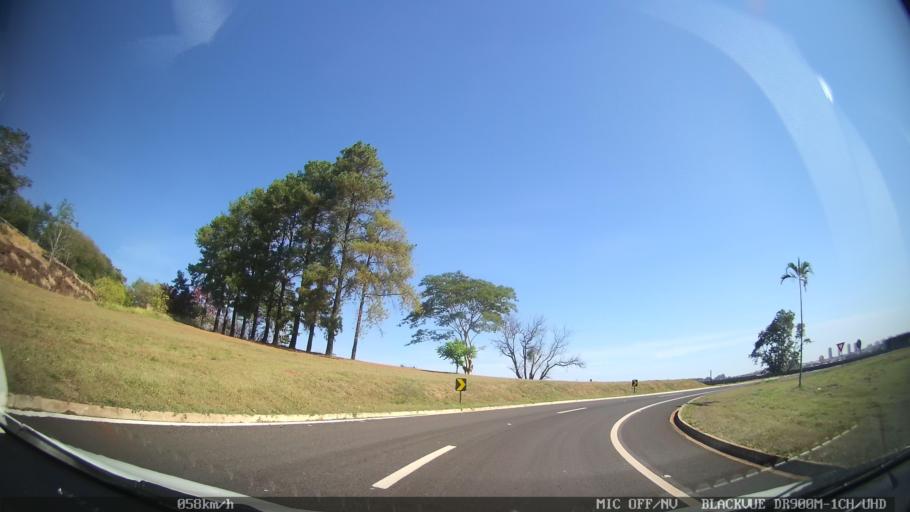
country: BR
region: Sao Paulo
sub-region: Ribeirao Preto
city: Ribeirao Preto
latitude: -21.2382
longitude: -47.7580
